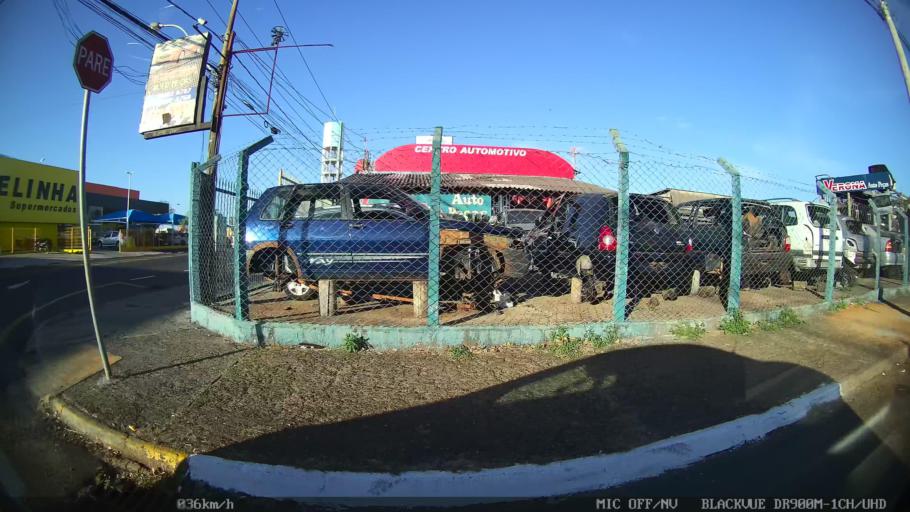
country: BR
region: Sao Paulo
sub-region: Franca
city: Franca
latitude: -20.5266
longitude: -47.3778
